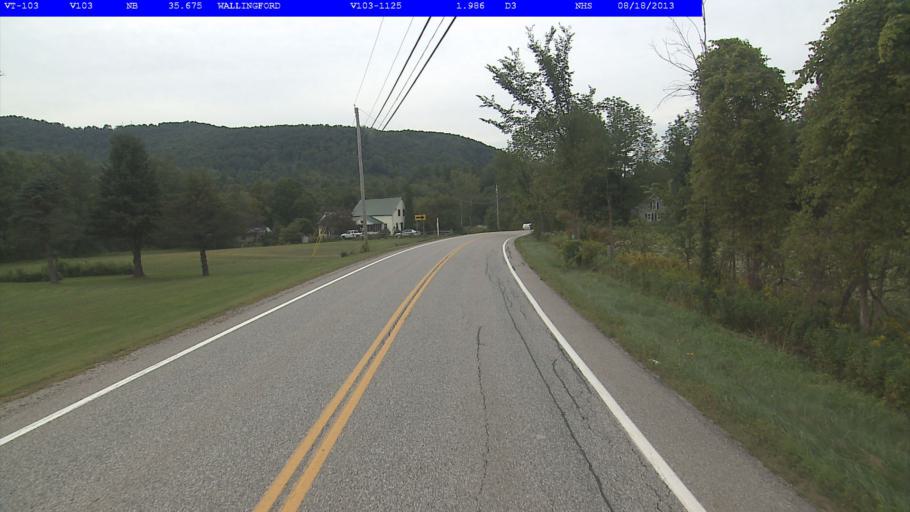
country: US
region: Vermont
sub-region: Rutland County
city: Rutland
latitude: 43.4728
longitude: -72.8888
